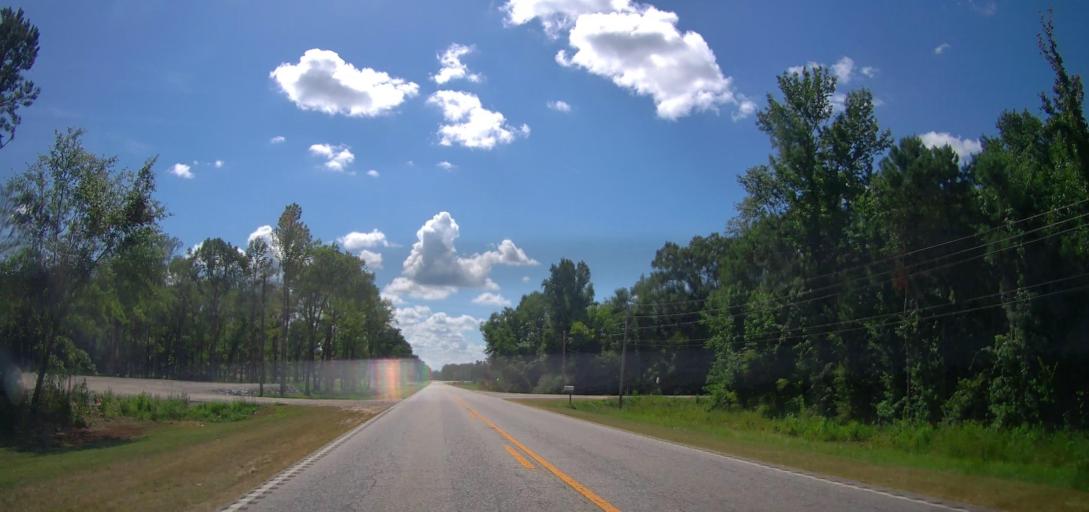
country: US
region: Alabama
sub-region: Elmore County
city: Tallassee
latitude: 32.3998
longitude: -85.9431
